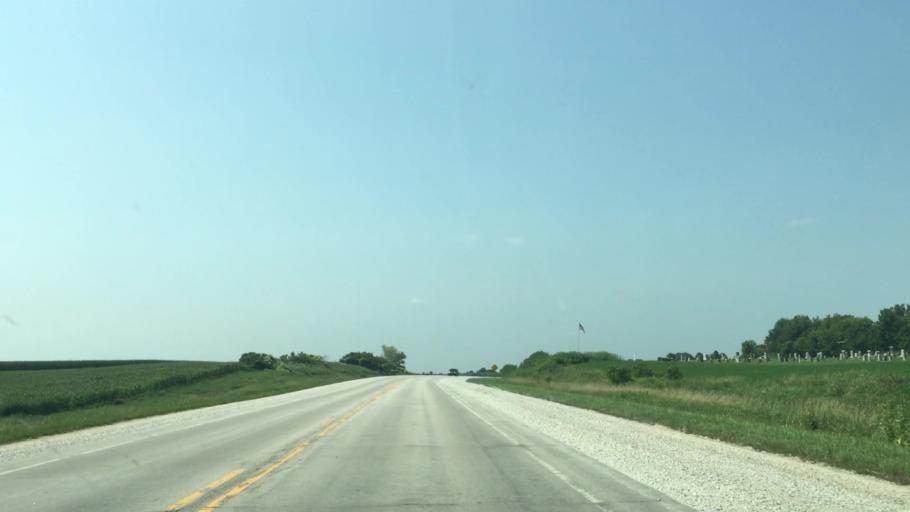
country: US
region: Iowa
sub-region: Winneshiek County
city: Decorah
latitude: 43.4521
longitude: -91.8665
